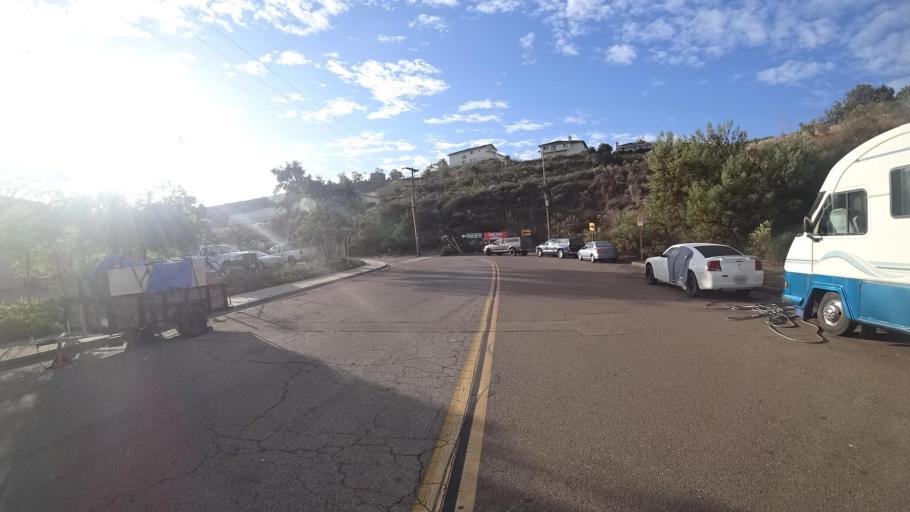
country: US
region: California
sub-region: San Diego County
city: La Presa
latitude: 32.7222
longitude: -116.9659
